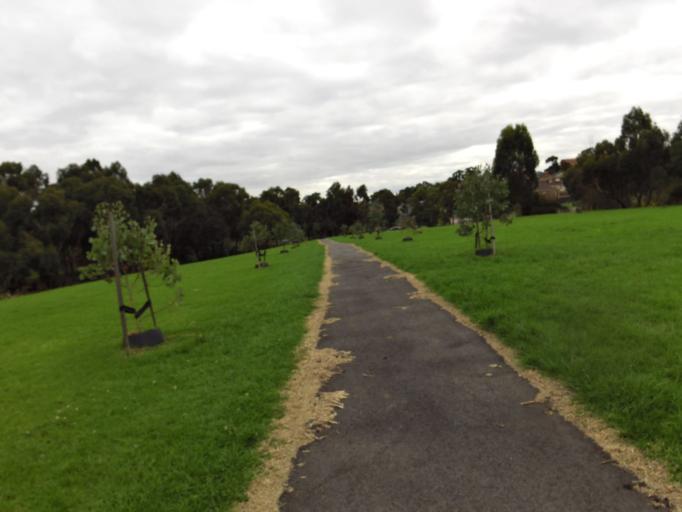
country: AU
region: Victoria
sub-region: Manningham
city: Donvale
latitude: -37.7645
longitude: 145.1633
